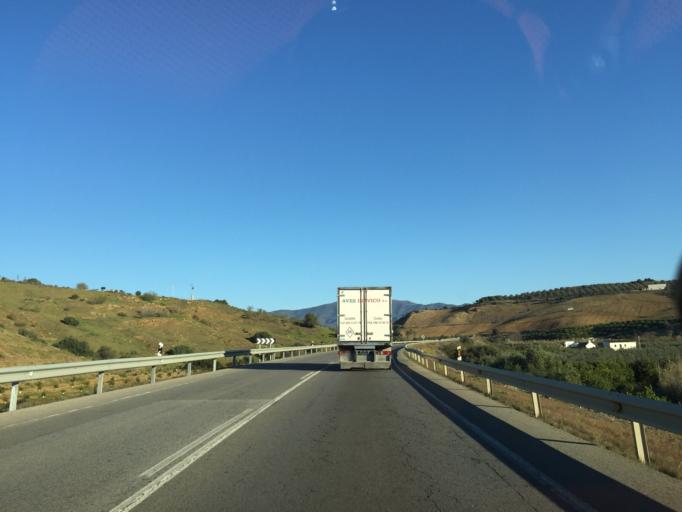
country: ES
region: Andalusia
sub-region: Provincia de Malaga
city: Pizarra
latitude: 36.7748
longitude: -4.7406
